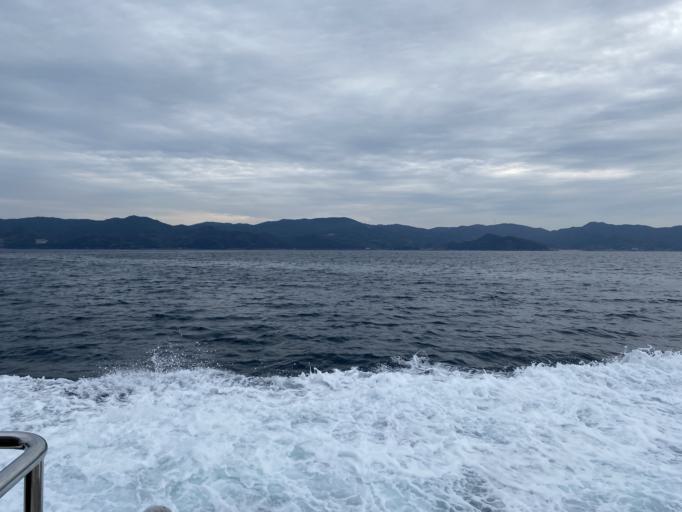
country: JP
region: Nagasaki
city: Nagasaki-shi
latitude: 32.6381
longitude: 129.7603
